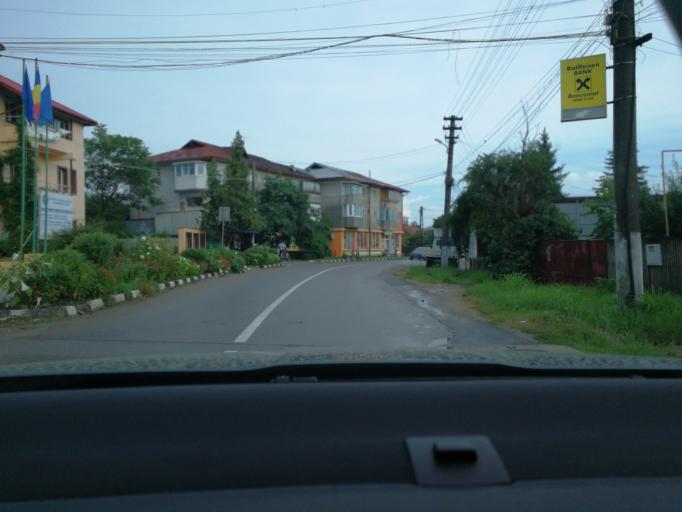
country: RO
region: Prahova
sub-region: Comuna Ceptura
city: Ceptura de Jos
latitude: 45.0183
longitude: 26.3278
